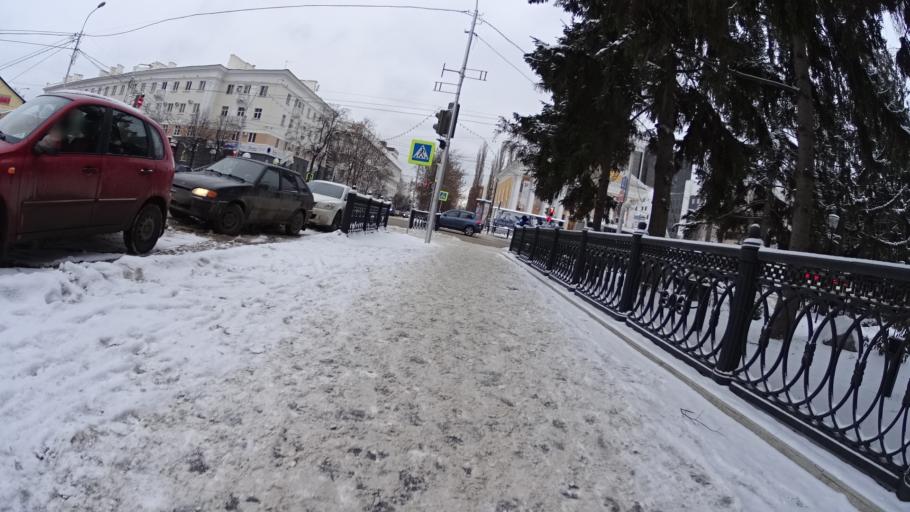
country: RU
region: Bashkortostan
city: Ufa
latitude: 54.7287
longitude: 55.9480
